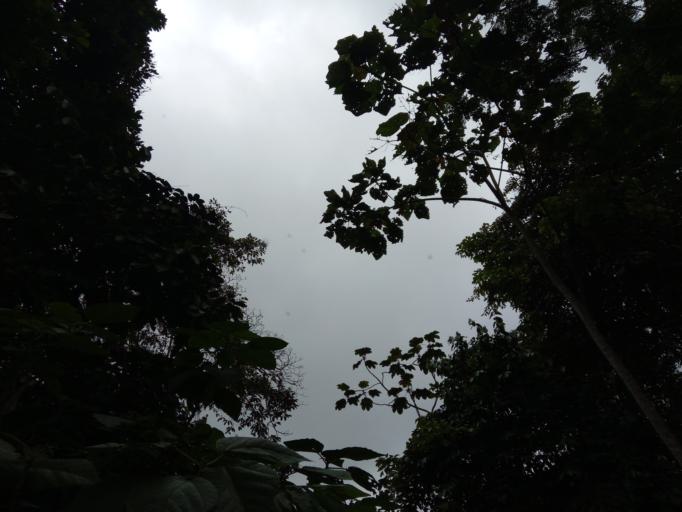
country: EC
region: Santo Domingo de los Tsachilas
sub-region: Canton Santo Domingo de los Colorados
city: Santo Domingo de los Colorados
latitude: -0.2333
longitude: -79.2083
